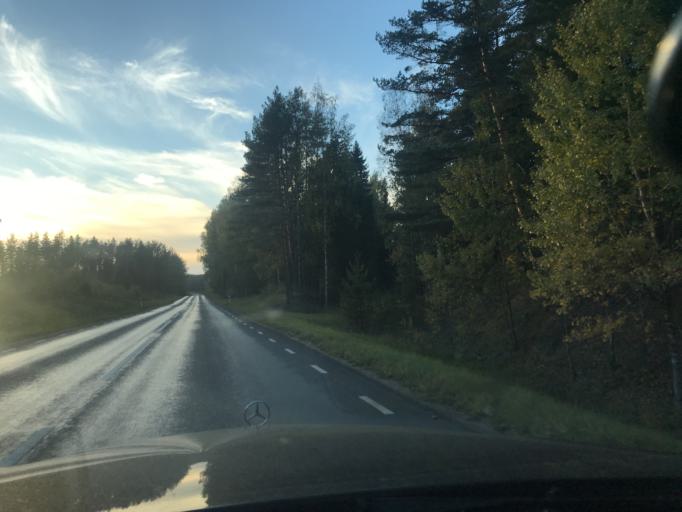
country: EE
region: Vorumaa
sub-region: Antsla vald
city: Vana-Antsla
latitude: 57.8821
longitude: 26.7485
